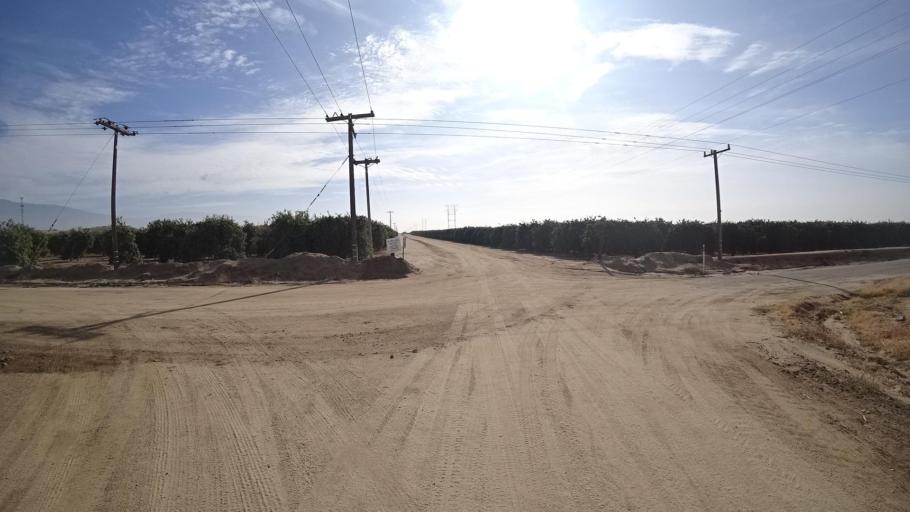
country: US
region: California
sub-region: Kern County
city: Arvin
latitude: 35.3112
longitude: -118.8073
